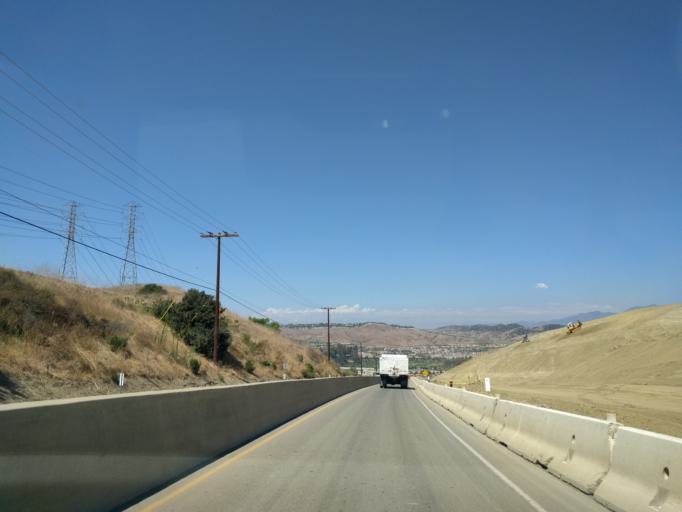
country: US
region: California
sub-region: Orange County
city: San Juan Capistrano
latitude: 33.5087
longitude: -117.6222
